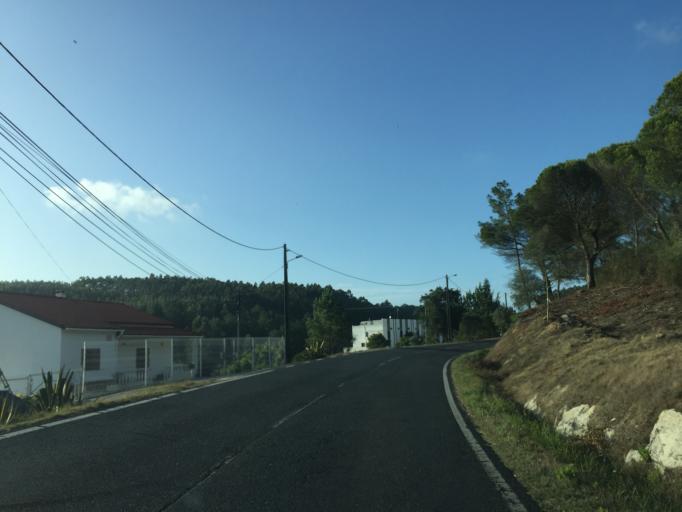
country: PT
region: Lisbon
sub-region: Torres Vedras
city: Torres Vedras
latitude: 39.1297
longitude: -9.2633
